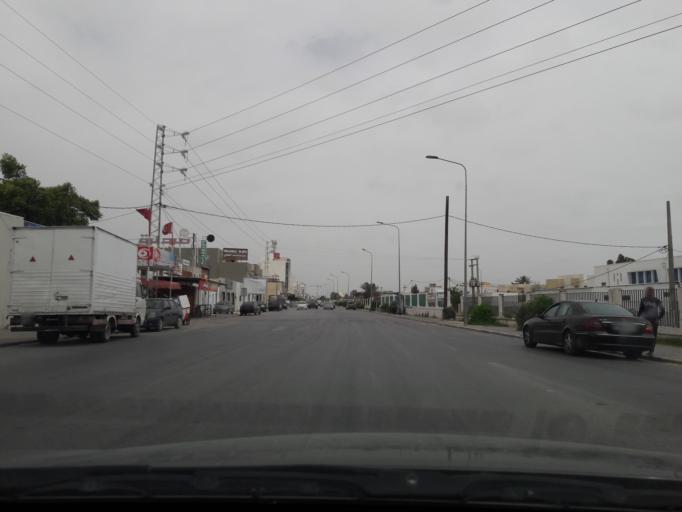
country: TN
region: Safaqis
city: Al Qarmadah
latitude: 34.7744
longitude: 10.7611
